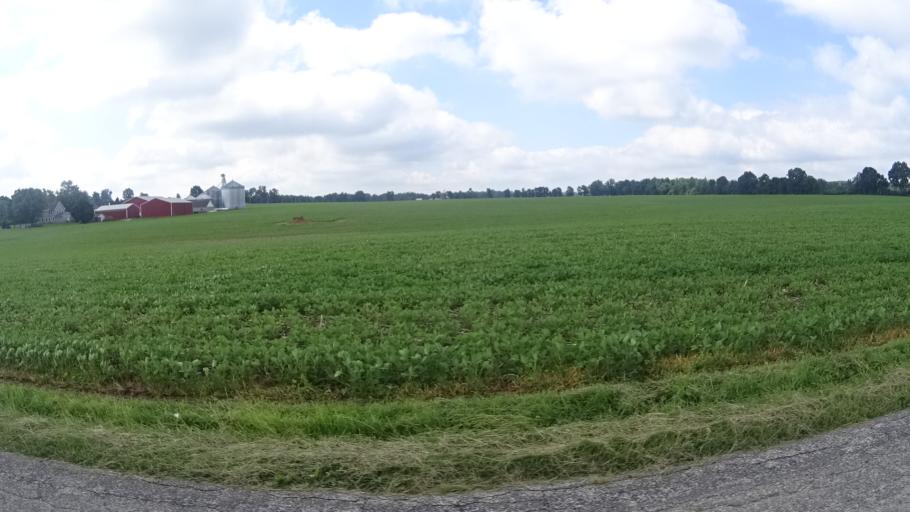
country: US
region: Ohio
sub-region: Huron County
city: Wakeman
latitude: 41.3058
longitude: -82.3899
